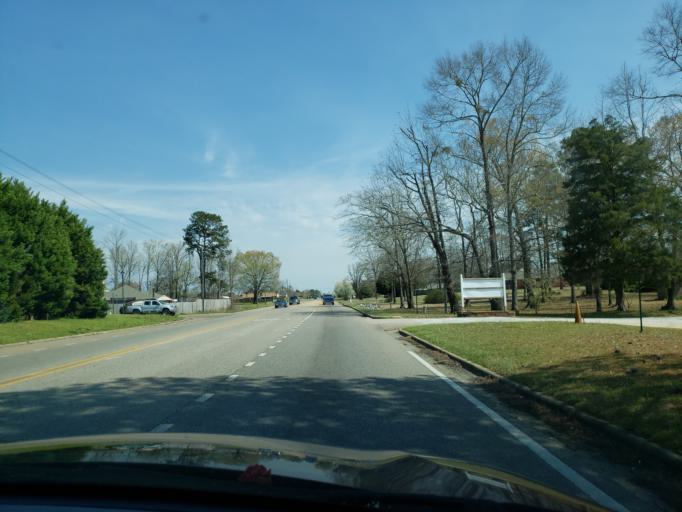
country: US
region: Alabama
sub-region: Elmore County
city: Coosada
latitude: 32.5262
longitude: -86.3591
